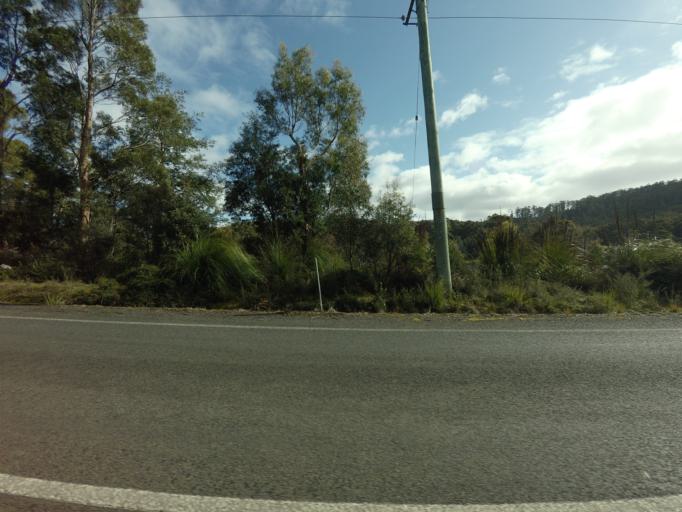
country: AU
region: Tasmania
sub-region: Huon Valley
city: Geeveston
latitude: -43.4127
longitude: 146.9418
